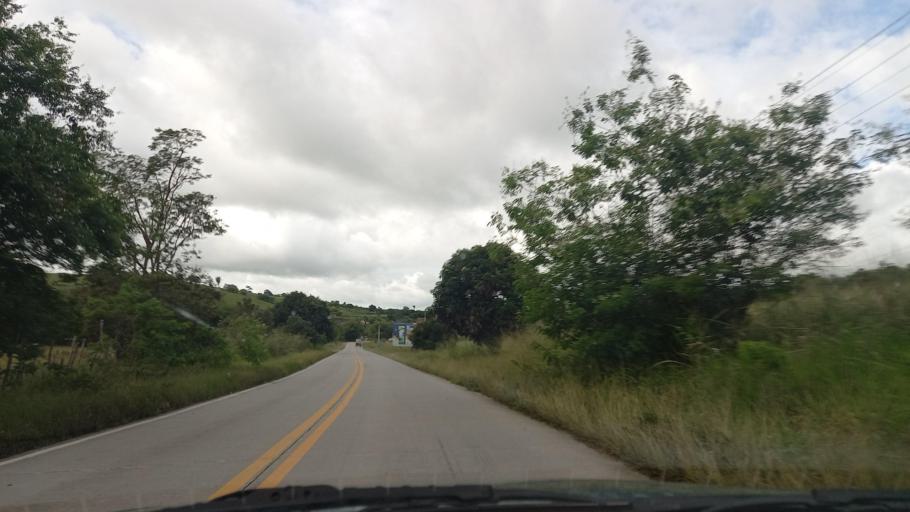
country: BR
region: Pernambuco
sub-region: Quipapa
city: Quipapa
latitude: -8.7885
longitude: -35.9638
